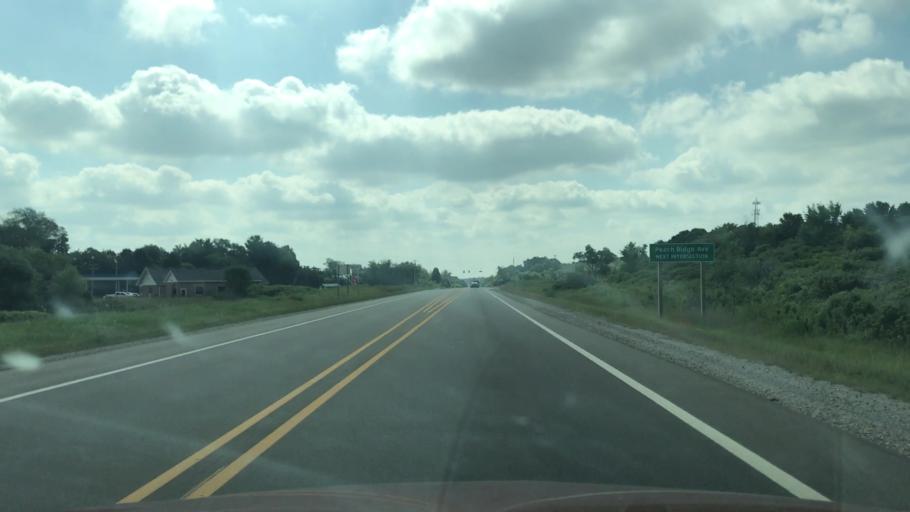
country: US
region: Michigan
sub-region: Kent County
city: Kent City
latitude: 43.2137
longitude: -85.7544
